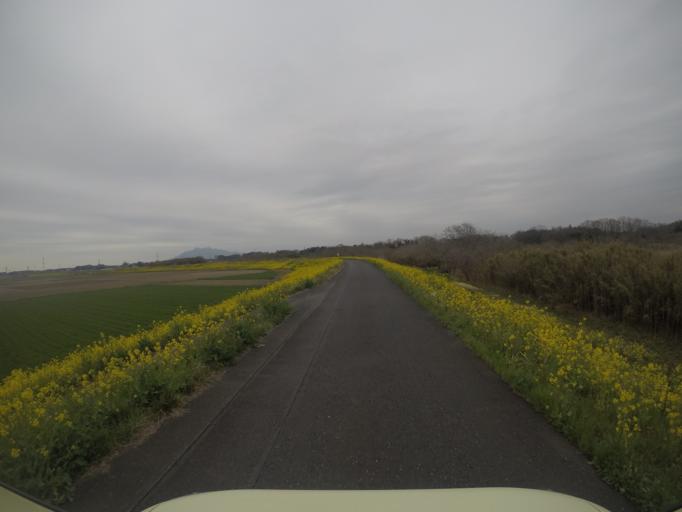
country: JP
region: Ibaraki
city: Ishige
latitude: 36.0952
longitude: 140.0030
